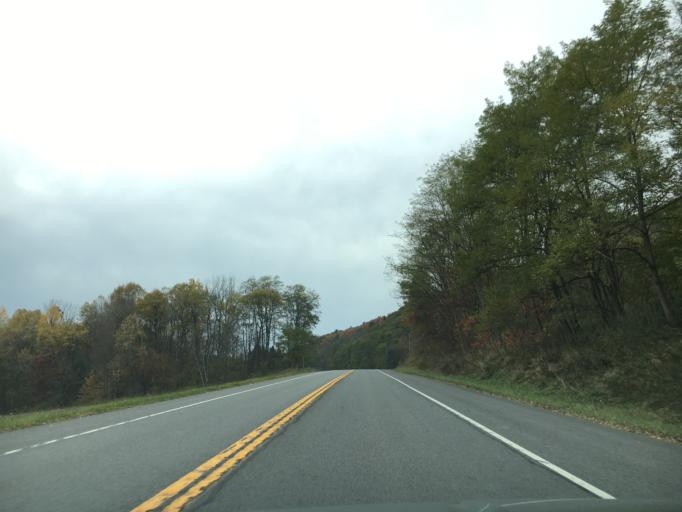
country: US
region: New York
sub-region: Otsego County
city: Oneonta
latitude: 42.5435
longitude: -74.9588
